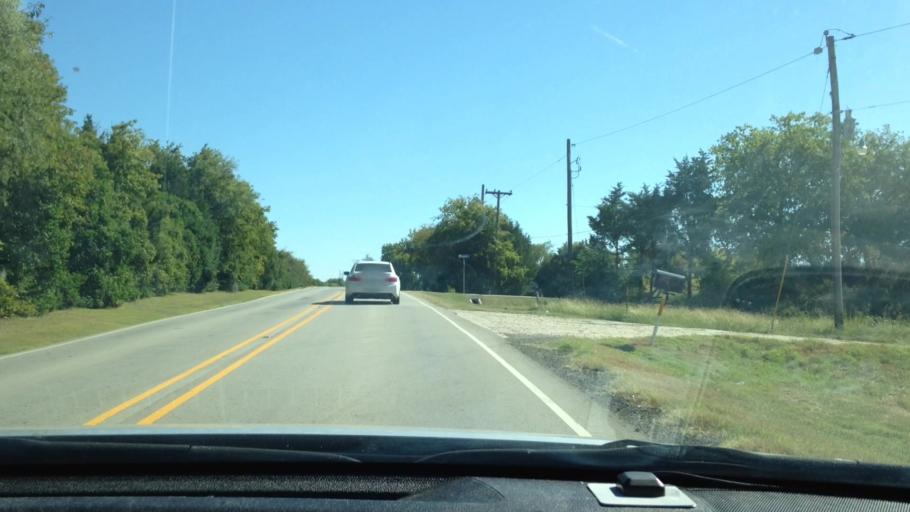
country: US
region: Texas
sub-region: Collin County
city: Lucas
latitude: 33.0714
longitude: -96.5713
